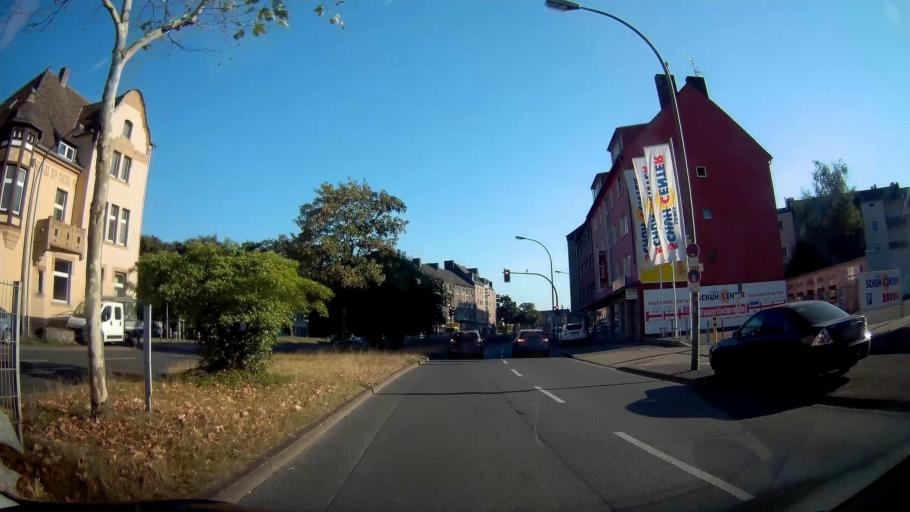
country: DE
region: North Rhine-Westphalia
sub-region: Regierungsbezirk Arnsberg
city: Dortmund
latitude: 51.5269
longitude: 7.4602
